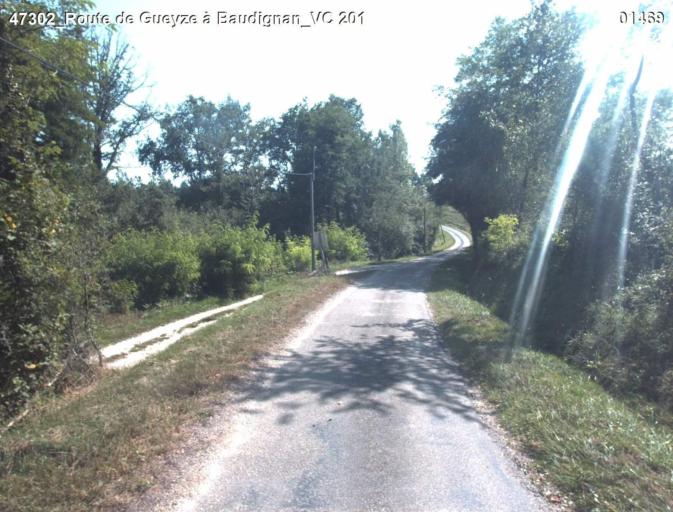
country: FR
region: Aquitaine
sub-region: Departement des Landes
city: Gabarret
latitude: 44.0536
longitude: 0.1196
